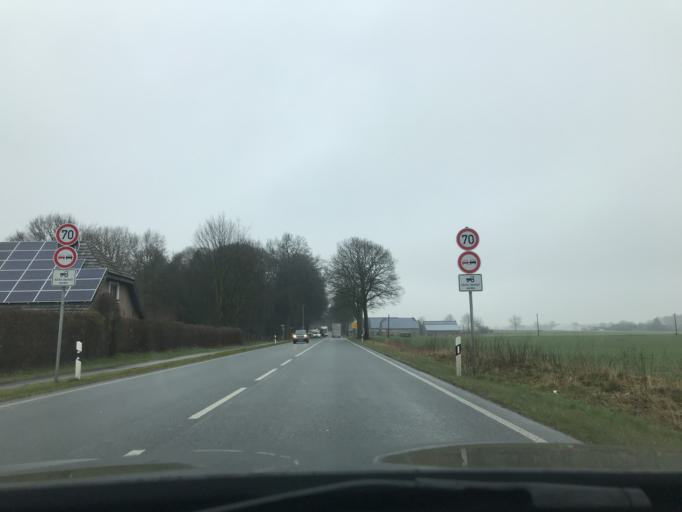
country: DE
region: North Rhine-Westphalia
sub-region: Regierungsbezirk Dusseldorf
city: Goch
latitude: 51.7337
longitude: 6.1596
